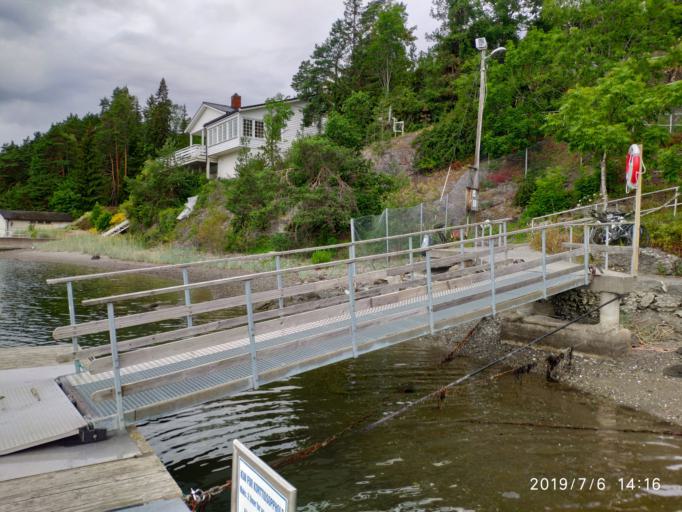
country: NO
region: Akershus
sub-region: Baerum
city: Sandvika
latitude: 59.8600
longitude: 10.5280
